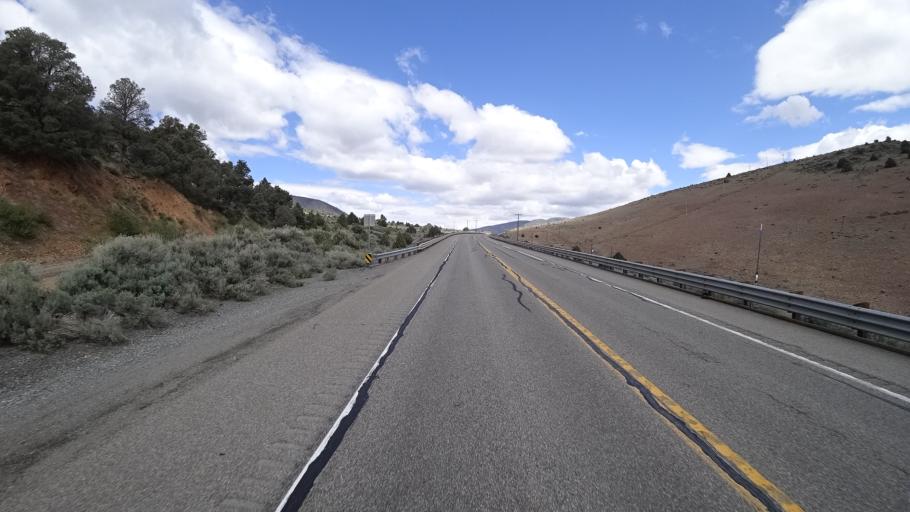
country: US
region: Nevada
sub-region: Lyon County
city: Smith Valley
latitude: 38.7079
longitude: -119.5527
